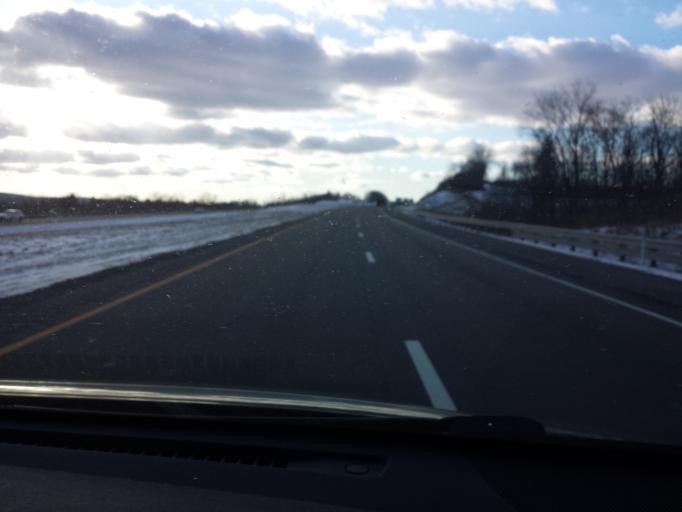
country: US
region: Pennsylvania
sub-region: Northumberland County
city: Riverside
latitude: 40.9881
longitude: -76.6907
